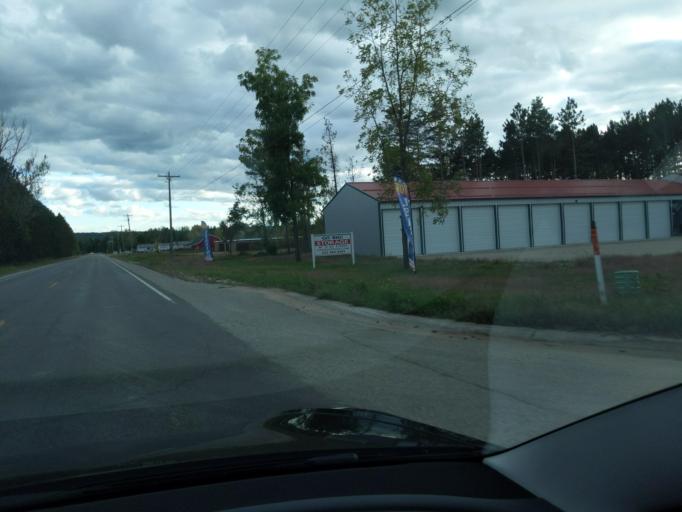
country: US
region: Michigan
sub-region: Kalkaska County
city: Rapid City
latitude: 44.8161
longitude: -85.2828
